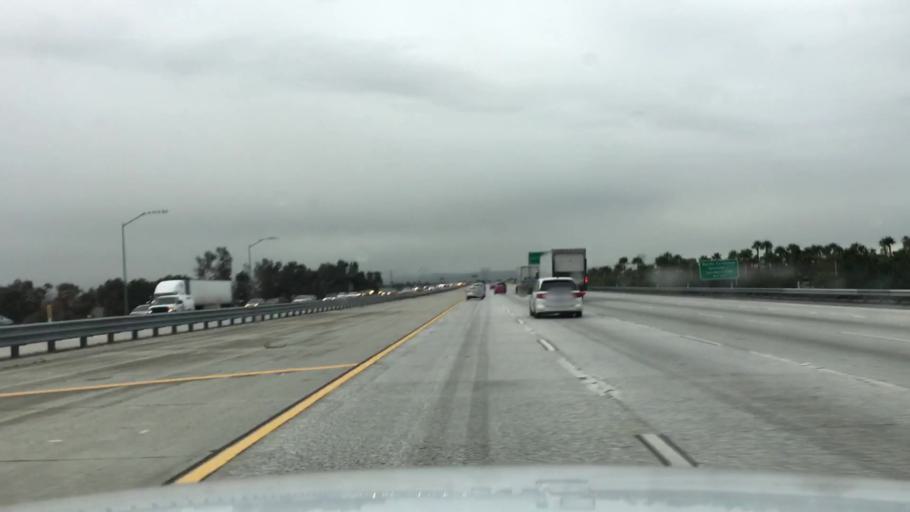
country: US
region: California
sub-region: San Bernardino County
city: Rancho Cucamonga
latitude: 34.1109
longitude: -117.5269
